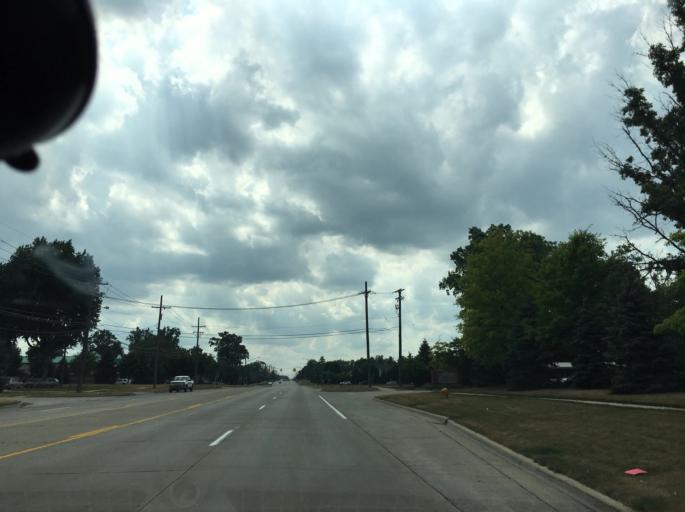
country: US
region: Michigan
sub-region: Macomb County
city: Fraser
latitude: 42.5532
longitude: -82.9672
